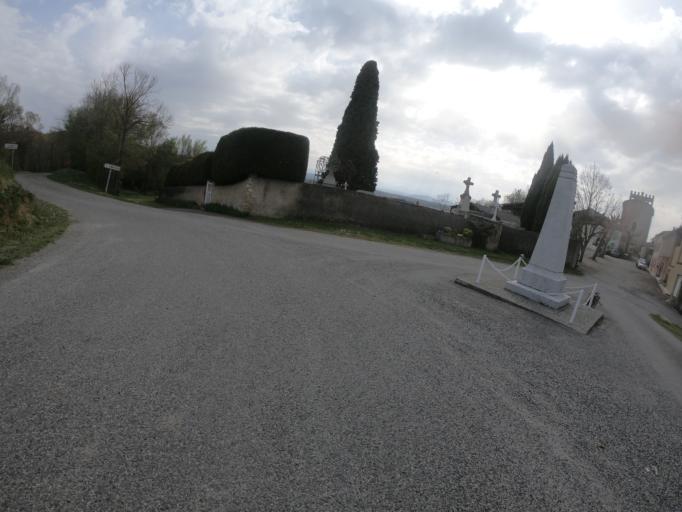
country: FR
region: Languedoc-Roussillon
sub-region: Departement de l'Aude
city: Belpech
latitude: 43.1312
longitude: 1.7491
